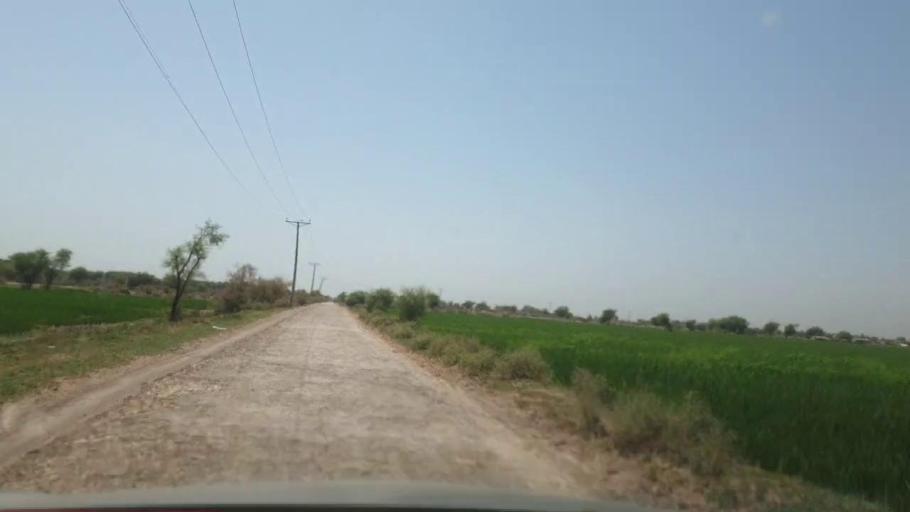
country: PK
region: Sindh
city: Warah
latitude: 27.4931
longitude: 67.7450
